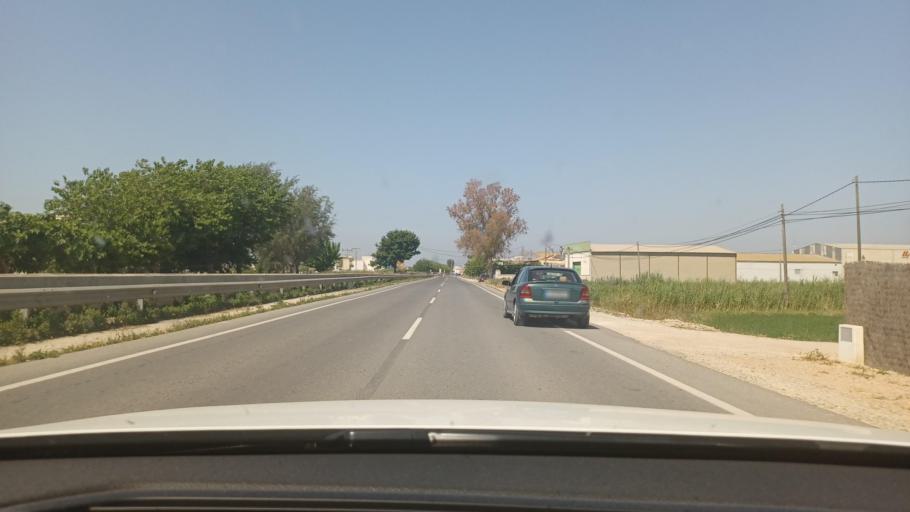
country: ES
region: Valencia
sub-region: Provincia de Alicante
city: Dolores
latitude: 38.1391
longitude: -0.7572
